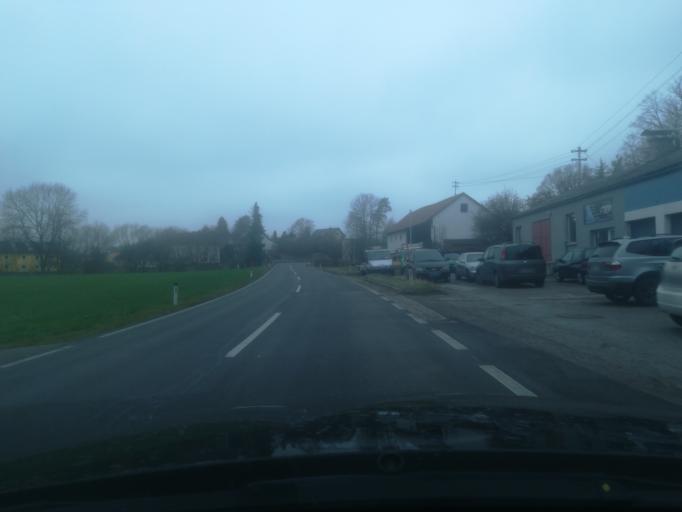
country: AT
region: Upper Austria
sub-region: Politischer Bezirk Perg
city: Perg
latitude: 48.3207
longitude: 14.5675
